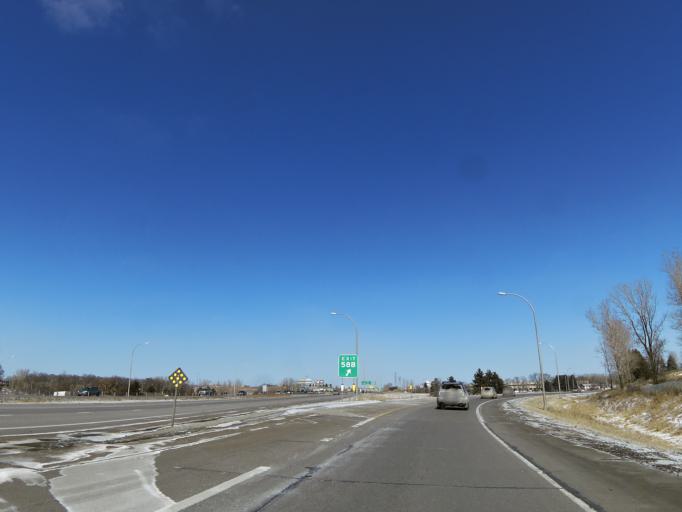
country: US
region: Minnesota
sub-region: Washington County
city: Oakdale
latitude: 44.9456
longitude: -92.9588
